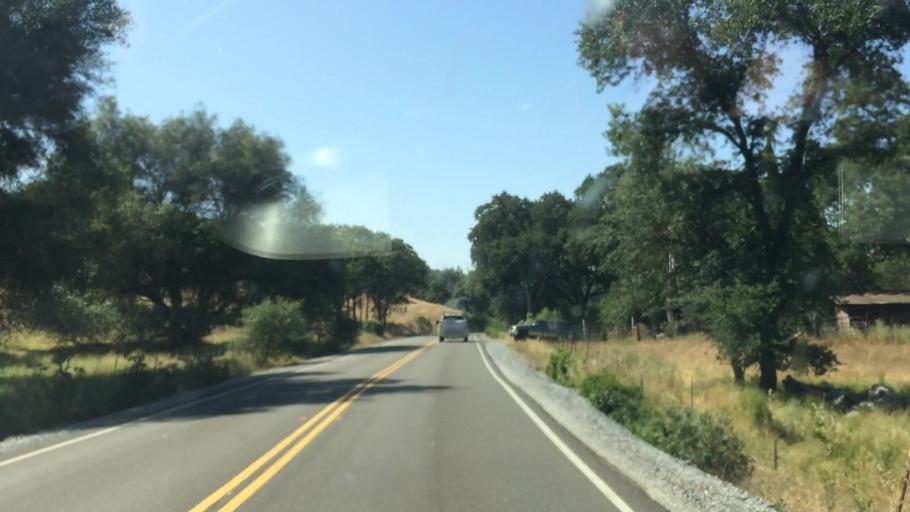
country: US
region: California
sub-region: Amador County
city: Plymouth
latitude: 38.5091
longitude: -120.9470
